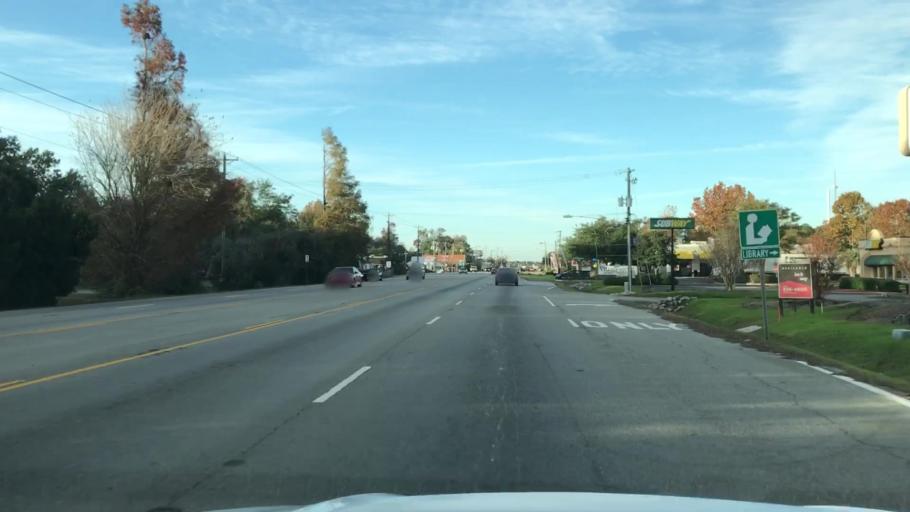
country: US
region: South Carolina
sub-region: Charleston County
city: North Charleston
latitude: 32.8052
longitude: -80.0119
